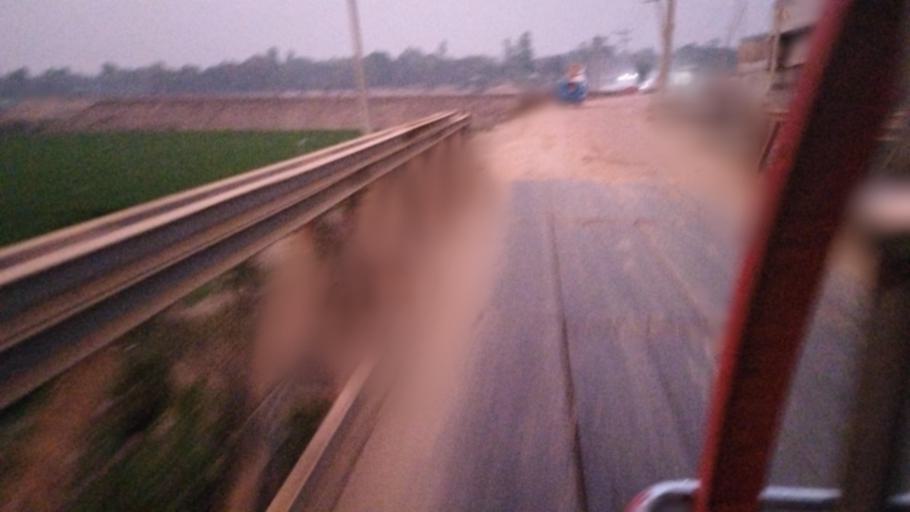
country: BD
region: Dhaka
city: Sakhipur
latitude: 24.3936
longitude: 90.3326
